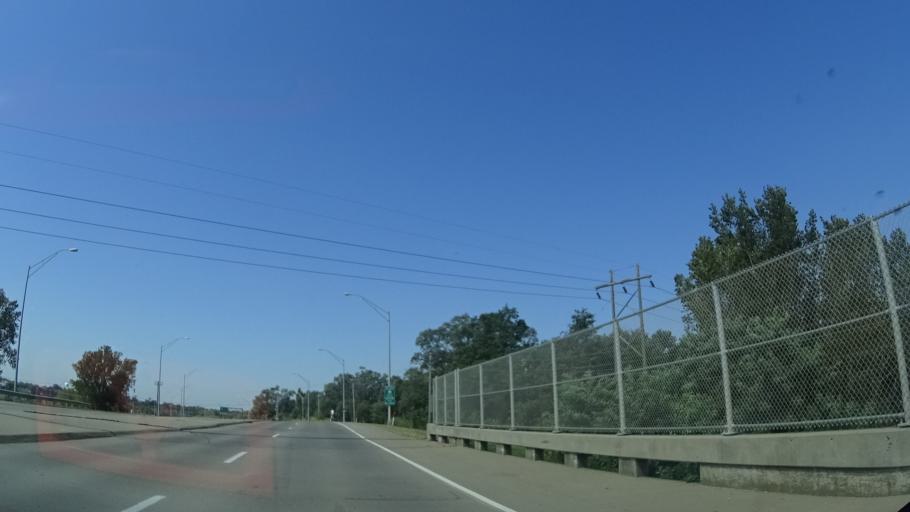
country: US
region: Nebraska
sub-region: Sarpy County
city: Offutt Air Force Base
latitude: 41.1166
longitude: -95.9299
